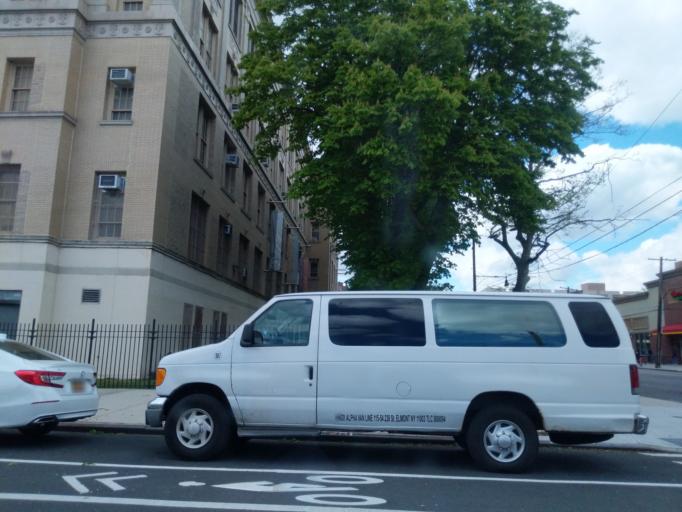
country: US
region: New York
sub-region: Bronx
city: The Bronx
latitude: 40.8753
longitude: -73.8606
